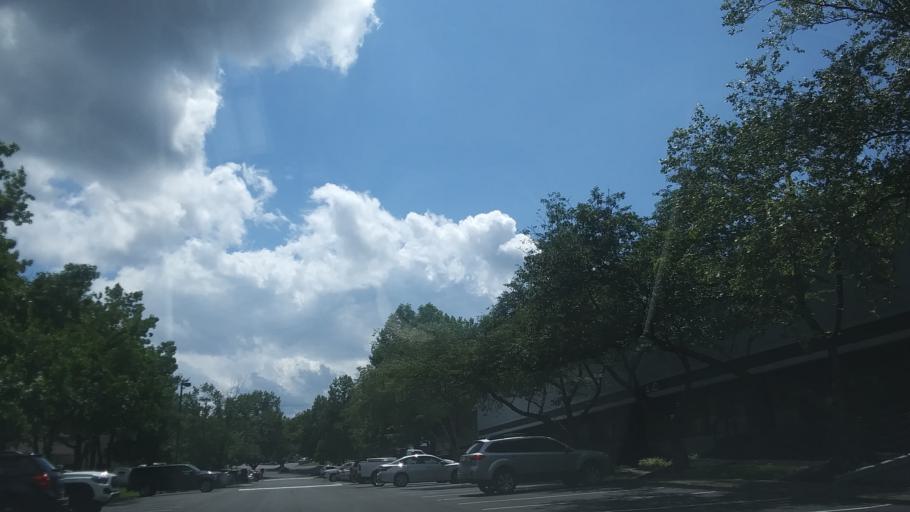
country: US
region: Tennessee
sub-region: Davidson County
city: Oak Hill
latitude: 36.0825
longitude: -86.6996
